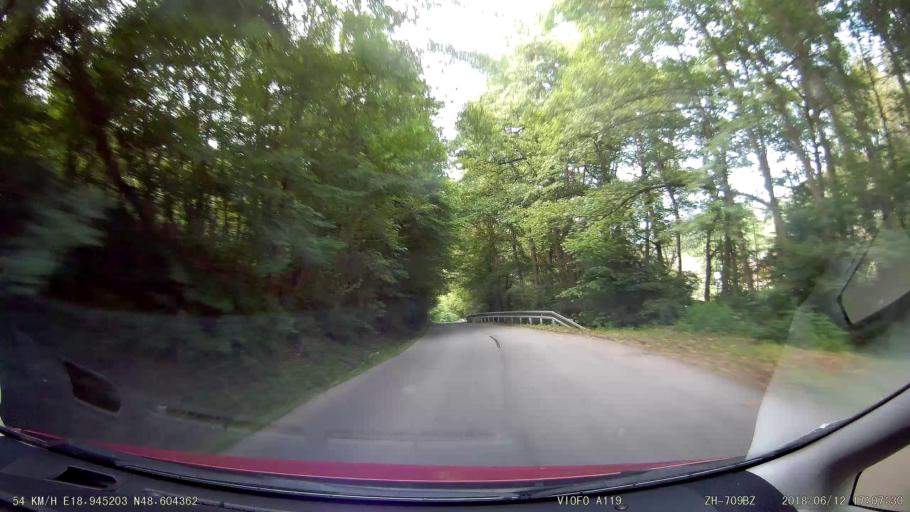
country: SK
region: Banskobystricky
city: Ziar nad Hronom
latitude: 48.6045
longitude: 18.9453
